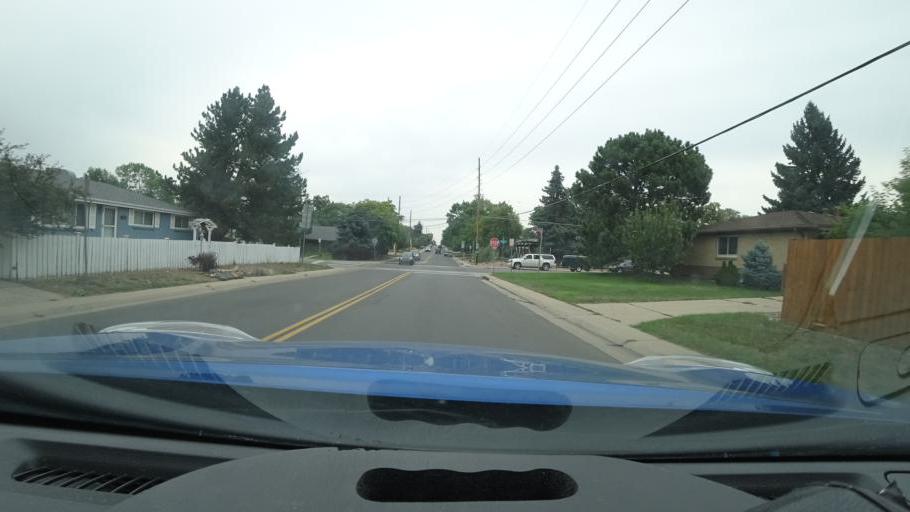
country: US
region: Colorado
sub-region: Arapahoe County
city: Glendale
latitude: 39.6817
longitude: -104.9317
